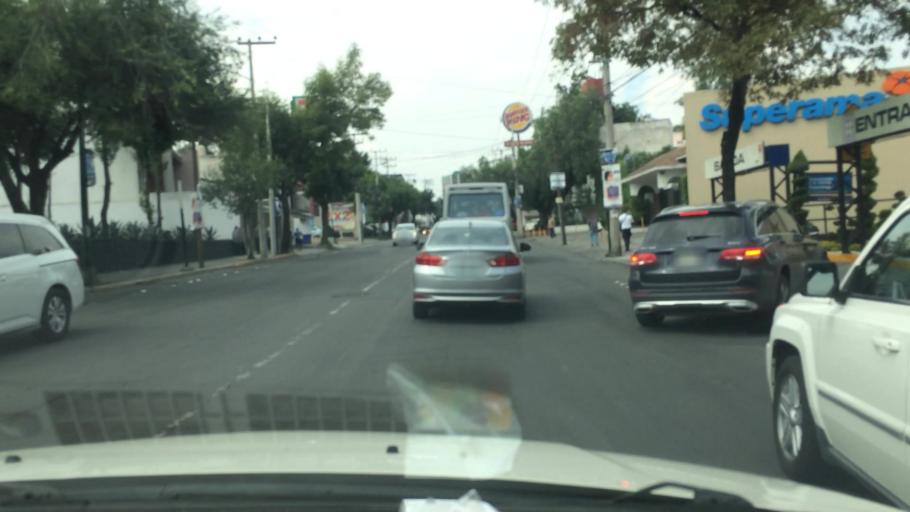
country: MX
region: Mexico City
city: Alvaro Obregon
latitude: 19.3580
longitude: -99.1984
